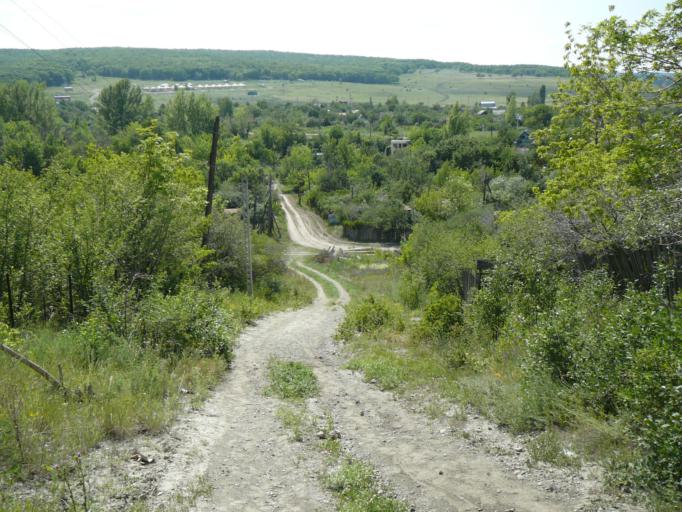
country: RU
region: Saratov
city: Sokolovyy
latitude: 51.5655
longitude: 45.8745
